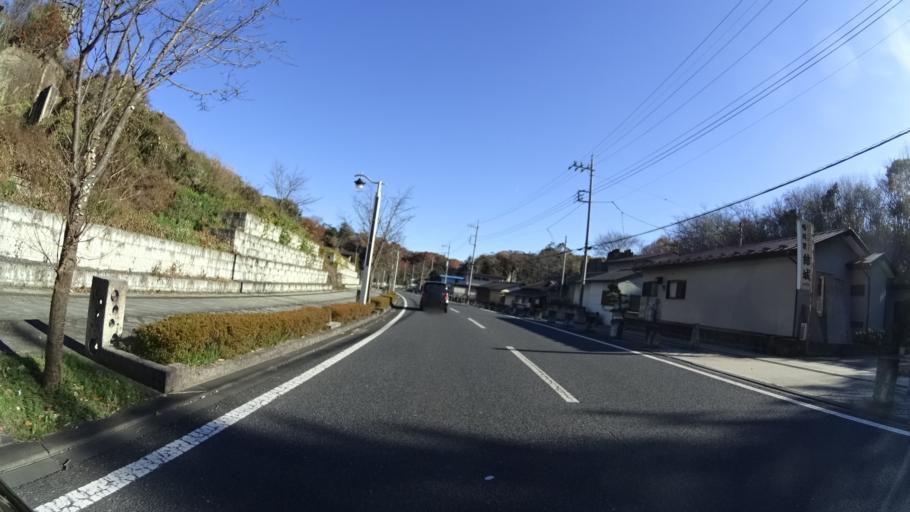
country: JP
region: Tochigi
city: Utsunomiya-shi
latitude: 36.6007
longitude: 139.8185
